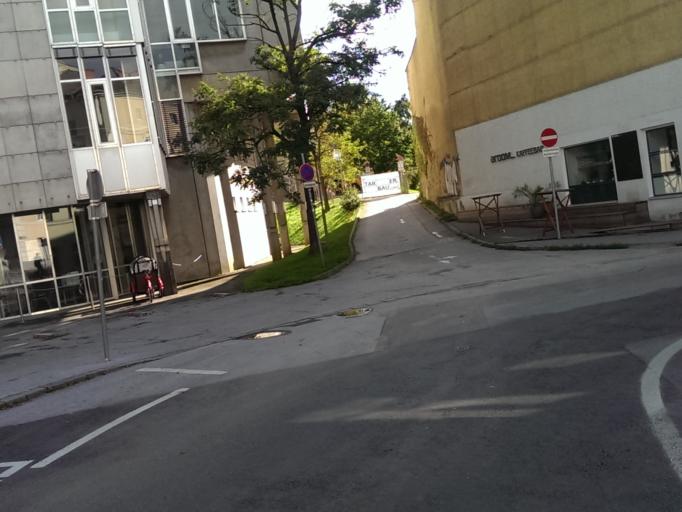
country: AT
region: Styria
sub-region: Graz Stadt
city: Graz
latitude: 47.0661
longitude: 15.4526
